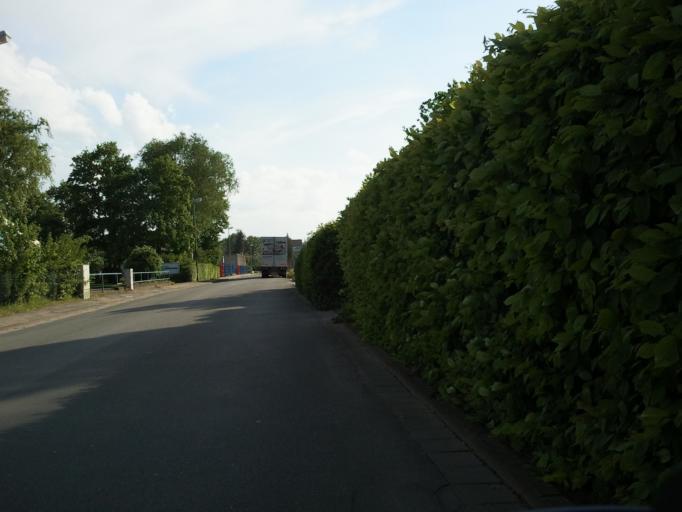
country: DE
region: Lower Saxony
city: Nienburg
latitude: 52.6222
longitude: 9.2323
